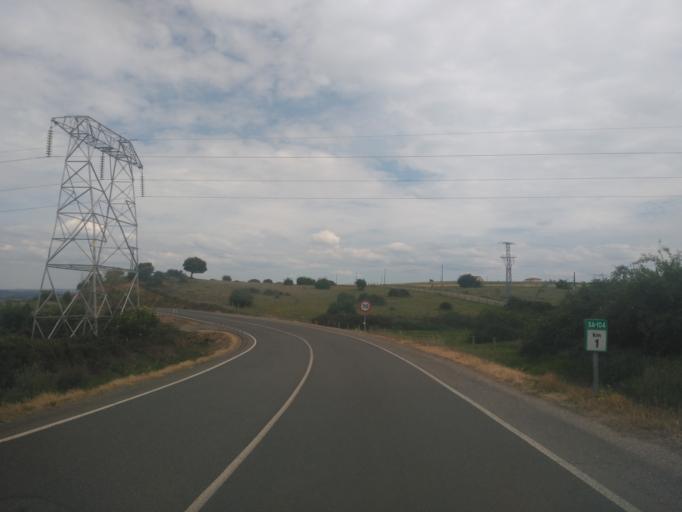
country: ES
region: Castille and Leon
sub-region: Provincia de Salamanca
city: Guijuelo
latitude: 40.5548
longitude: -5.6626
